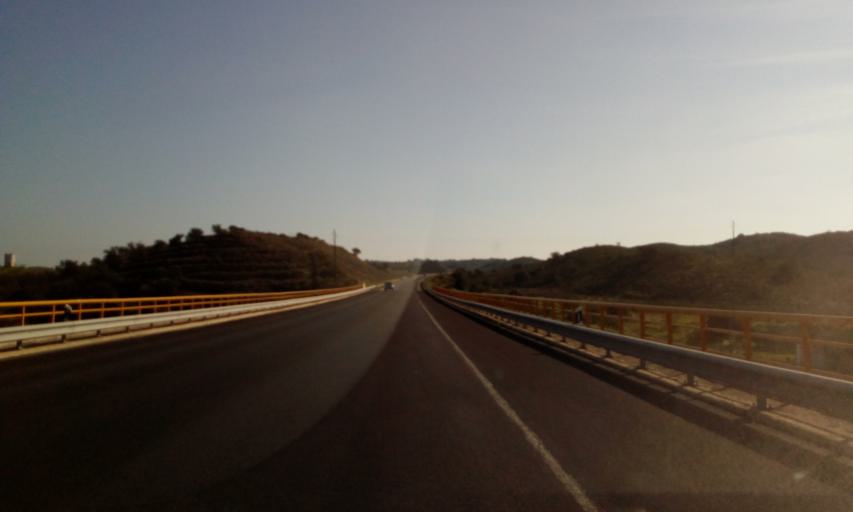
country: PT
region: Faro
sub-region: Castro Marim
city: Castro Marim
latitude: 37.2536
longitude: -7.4792
